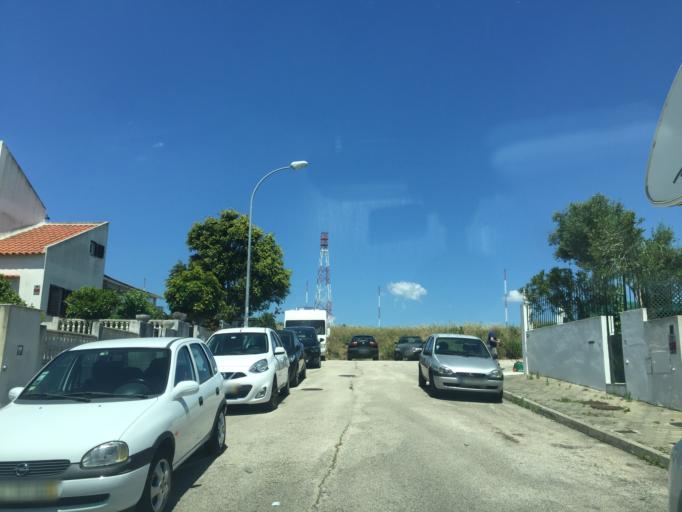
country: PT
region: Lisbon
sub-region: Oeiras
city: Quejas
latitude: 38.7242
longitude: -9.2682
